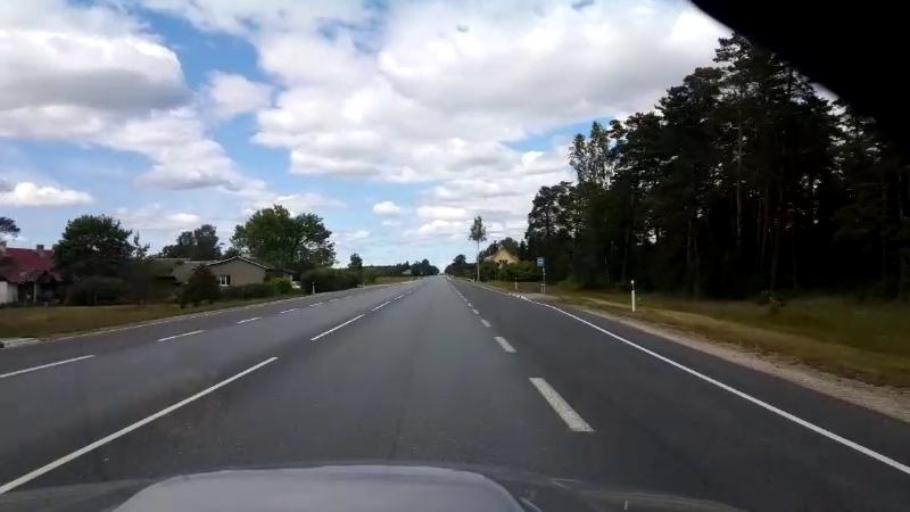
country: EE
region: Raplamaa
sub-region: Maerjamaa vald
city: Marjamaa
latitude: 58.9783
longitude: 24.4737
